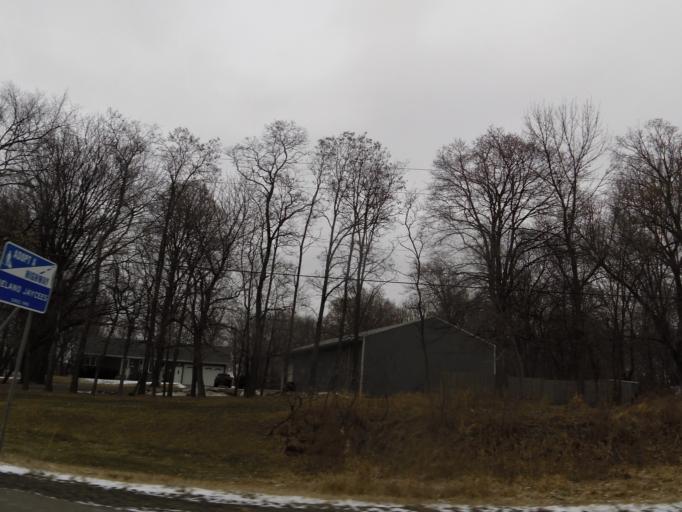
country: US
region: Minnesota
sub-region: Wright County
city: Delano
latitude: 45.0636
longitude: -93.8106
